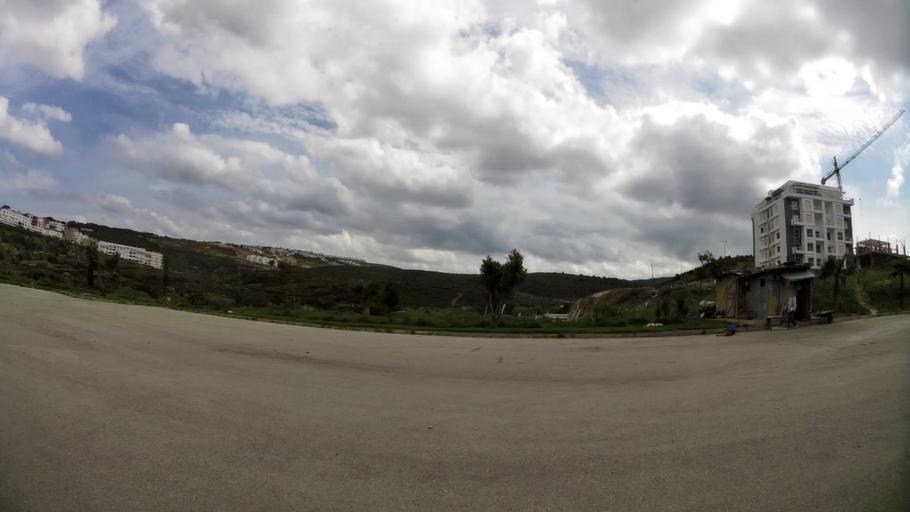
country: MA
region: Tanger-Tetouan
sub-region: Tanger-Assilah
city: Tangier
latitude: 35.7843
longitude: -5.7547
